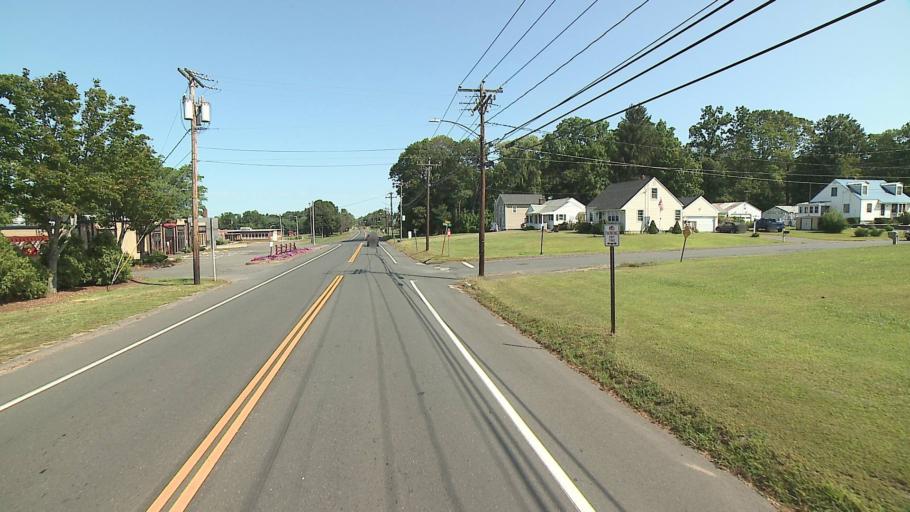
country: US
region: Connecticut
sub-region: Hartford County
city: Windsor Locks
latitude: 41.9418
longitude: -72.6032
